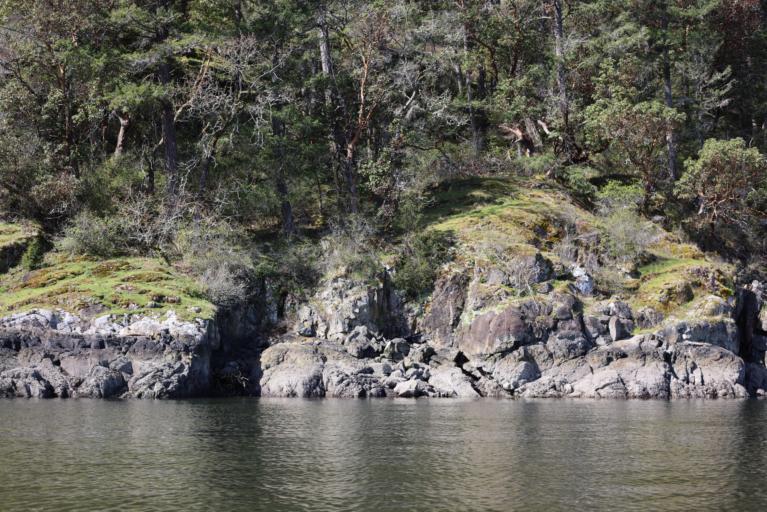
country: CA
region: British Columbia
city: Langford
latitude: 48.5687
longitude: -123.5141
